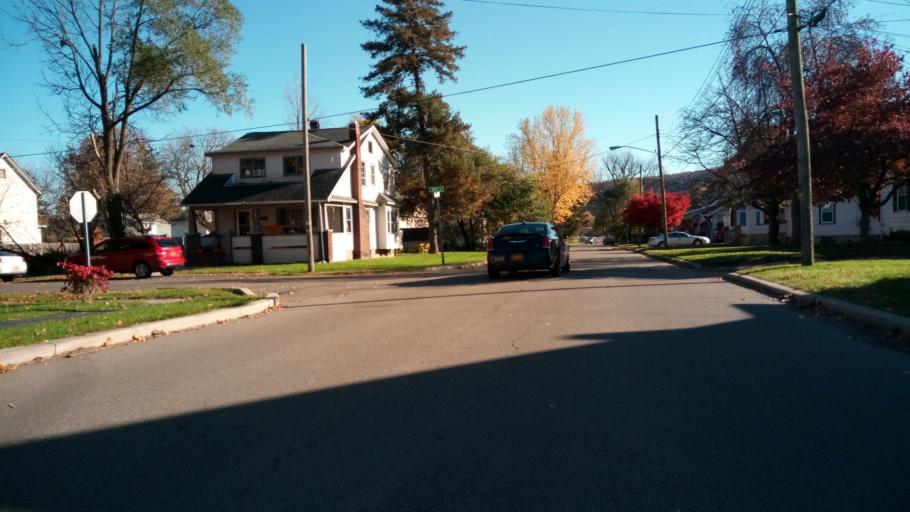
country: US
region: New York
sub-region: Chemung County
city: Southport
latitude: 42.0651
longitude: -76.8109
